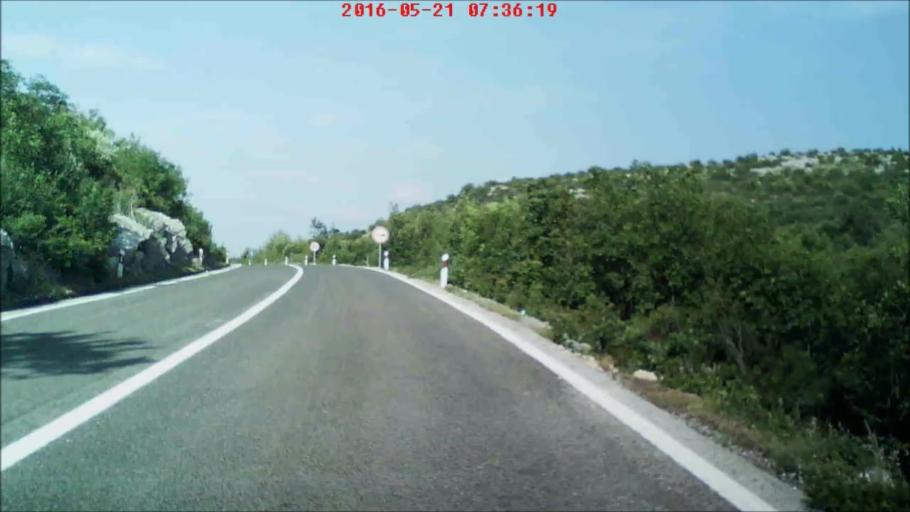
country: HR
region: Dubrovacko-Neretvanska
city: Podgora
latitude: 42.7879
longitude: 17.8672
